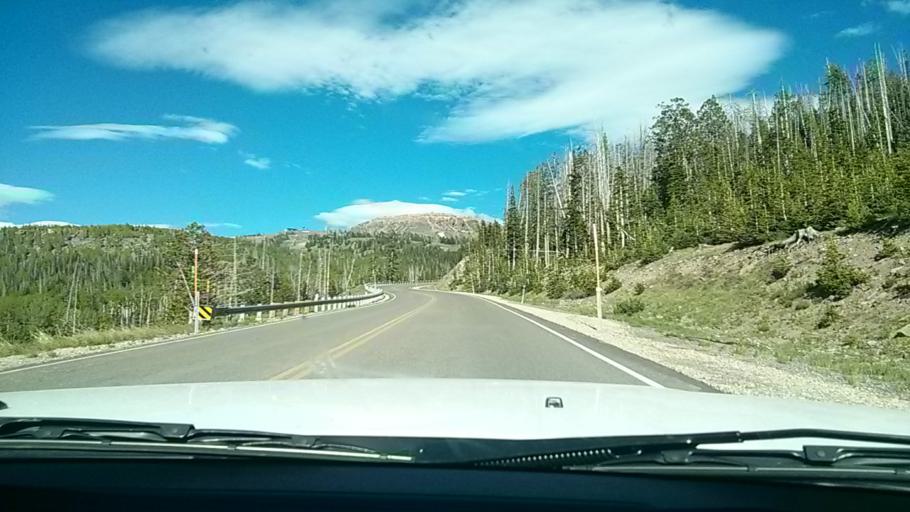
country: US
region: Utah
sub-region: Iron County
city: Parowan
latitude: 37.6811
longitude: -112.8543
